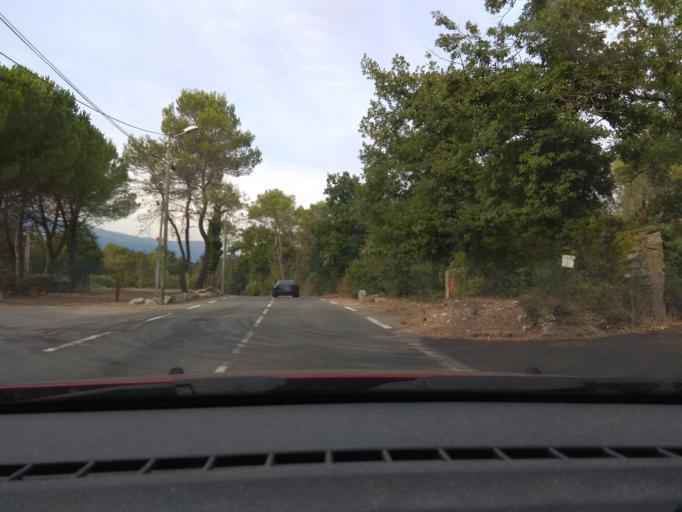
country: FR
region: Provence-Alpes-Cote d'Azur
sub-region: Departement des Alpes-Maritimes
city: Valbonne
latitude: 43.6484
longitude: 7.0230
